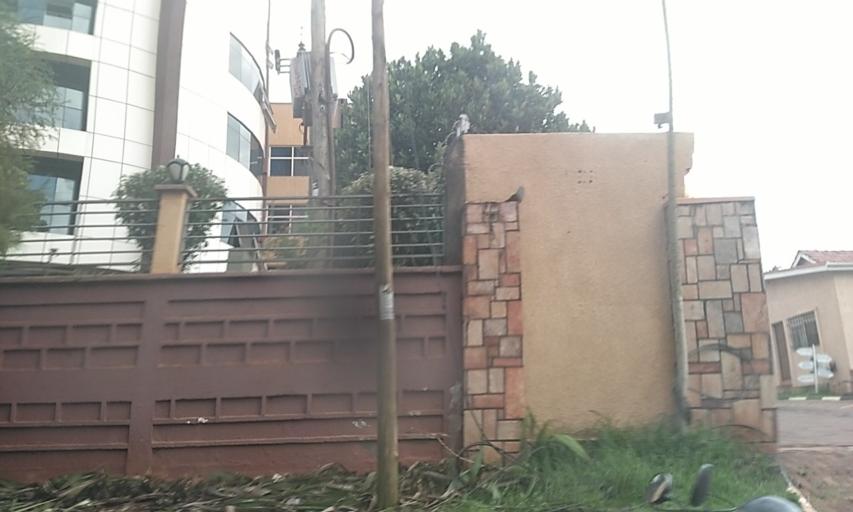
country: UG
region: Central Region
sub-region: Kampala District
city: Kampala
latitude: 0.3232
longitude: 32.5935
